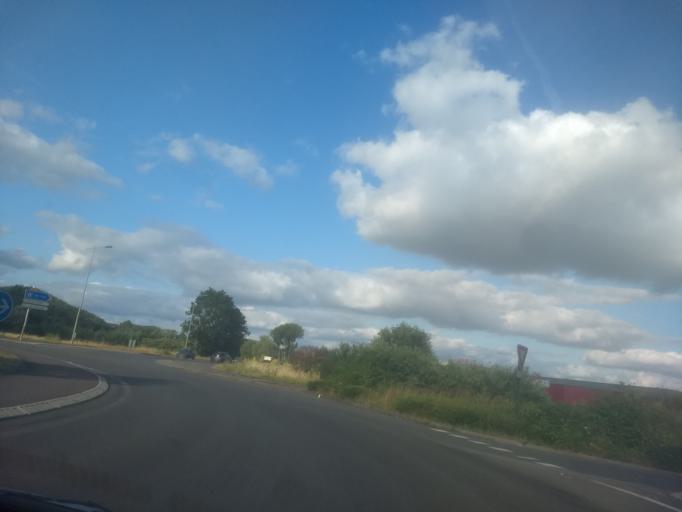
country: FR
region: Nord-Pas-de-Calais
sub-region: Departement du Pas-de-Calais
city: Carvin
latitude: 50.4798
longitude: 2.9660
